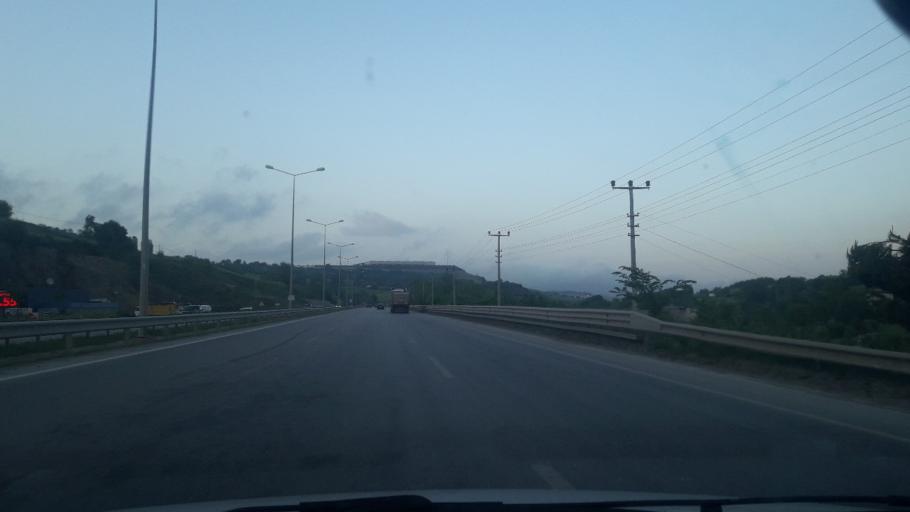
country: TR
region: Samsun
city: Samsun
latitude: 41.2876
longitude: 36.2025
